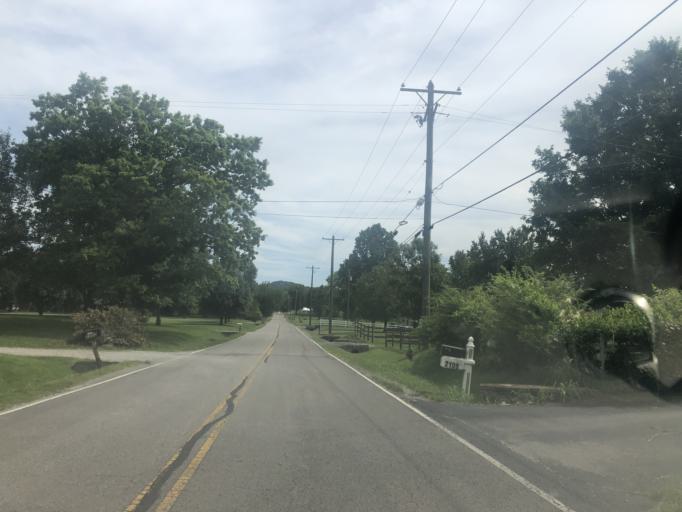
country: US
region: Tennessee
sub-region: Davidson County
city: Lakewood
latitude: 36.2037
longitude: -86.6643
